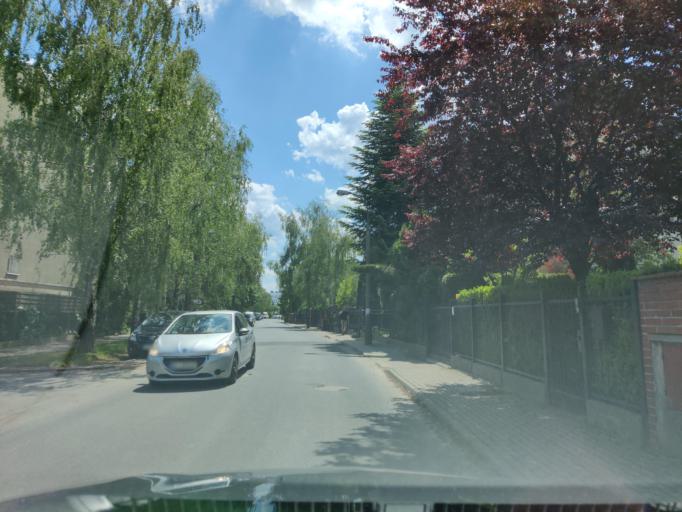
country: PL
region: Masovian Voivodeship
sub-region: Warszawa
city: Ursynow
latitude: 52.1449
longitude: 21.0152
